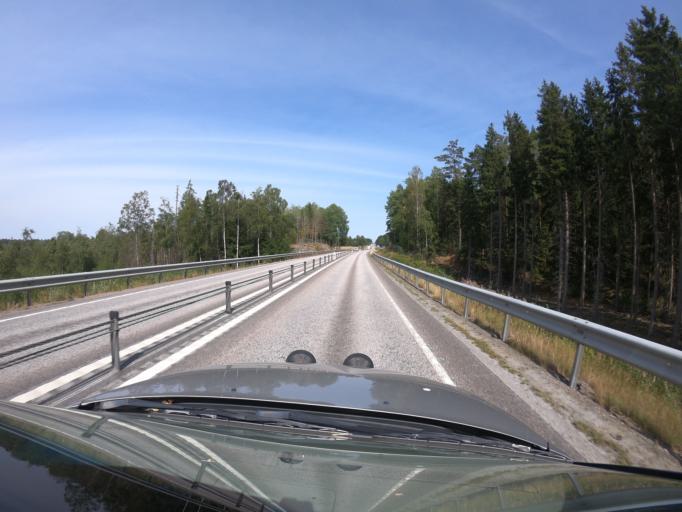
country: SE
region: Kronoberg
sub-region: Vaxjo Kommun
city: Braas
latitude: 57.0303
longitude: 15.0650
